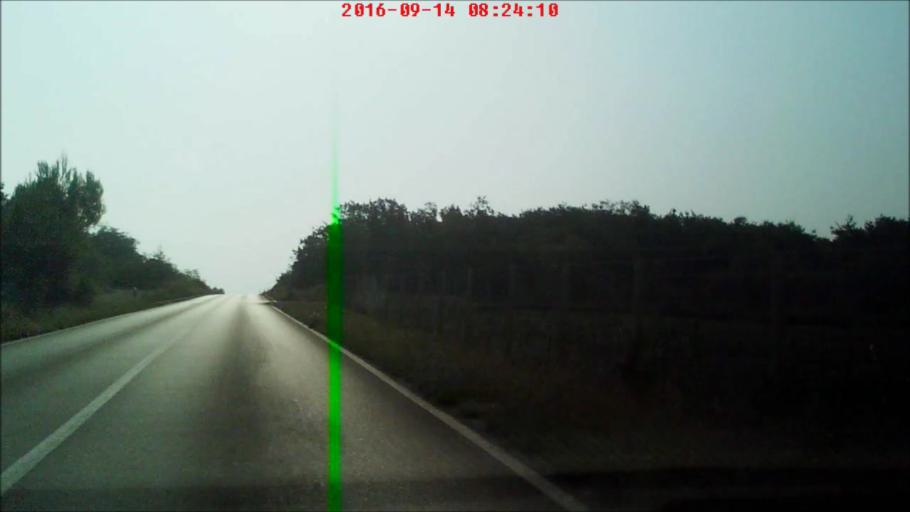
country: HR
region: Zadarska
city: Vrsi
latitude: 44.2078
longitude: 15.2403
